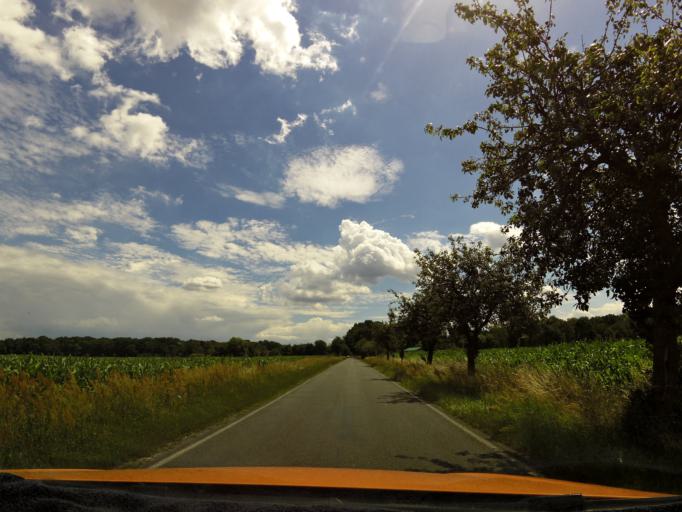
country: DE
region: Brandenburg
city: Storkow
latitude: 52.2435
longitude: 13.9017
